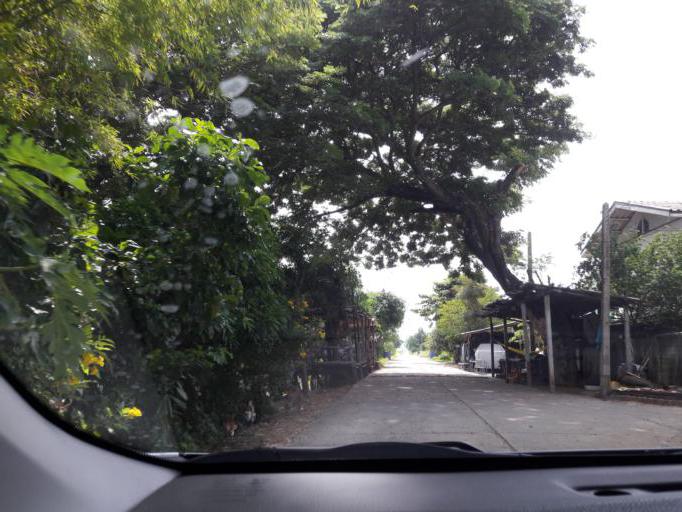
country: TH
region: Ang Thong
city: Ang Thong
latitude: 14.5749
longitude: 100.4547
